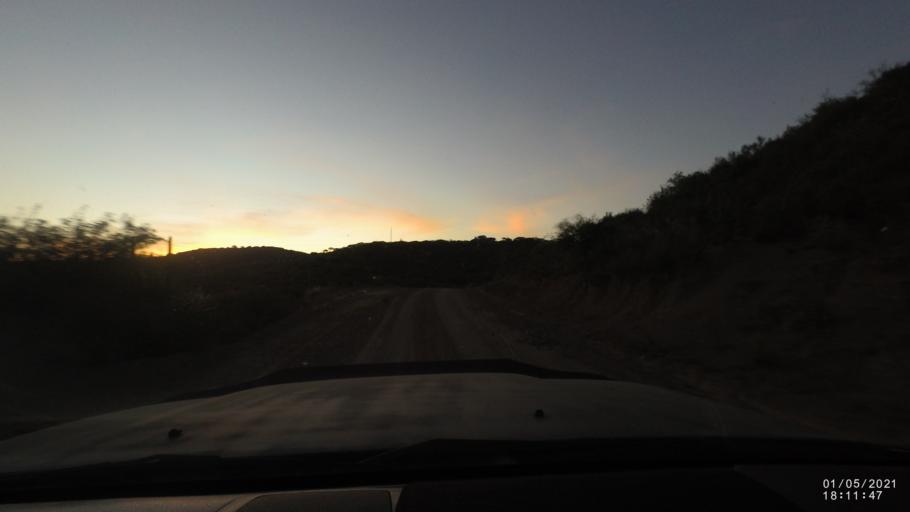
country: BO
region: Cochabamba
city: Capinota
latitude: -17.6804
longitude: -66.2008
